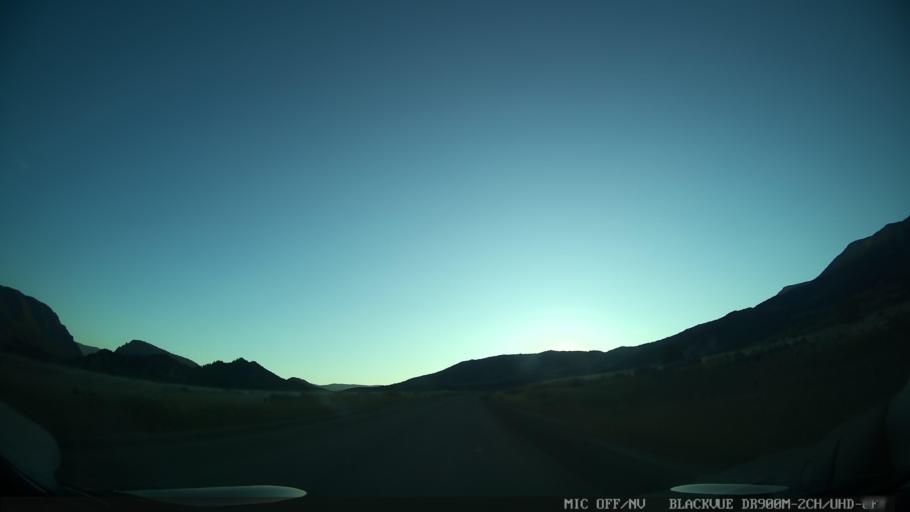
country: US
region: Colorado
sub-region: Eagle County
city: Edwards
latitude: 39.8997
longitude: -106.6045
